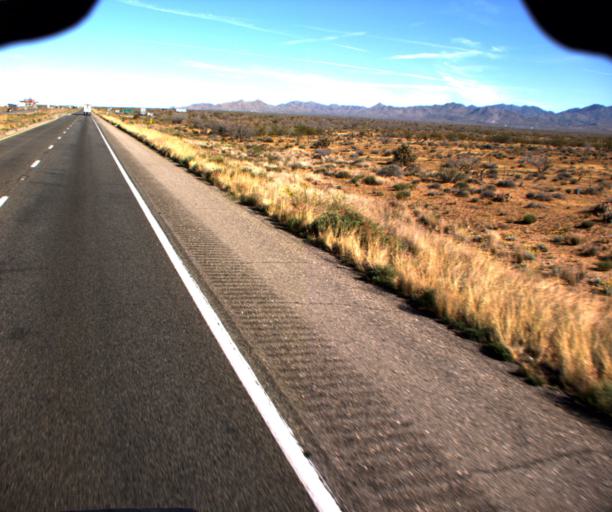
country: US
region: Arizona
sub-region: Mohave County
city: Golden Valley
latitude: 35.3295
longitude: -114.2104
